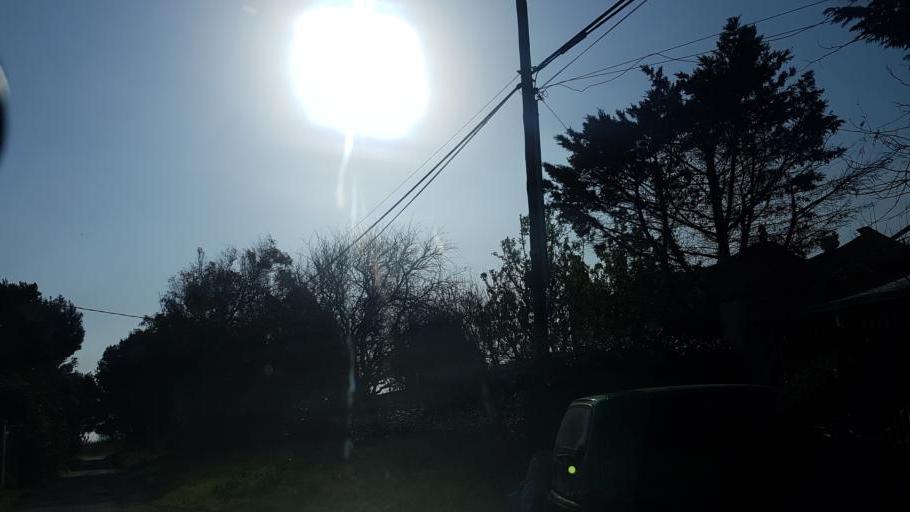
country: IT
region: Apulia
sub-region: Provincia di Brindisi
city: Materdomini
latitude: 40.6690
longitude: 17.9456
